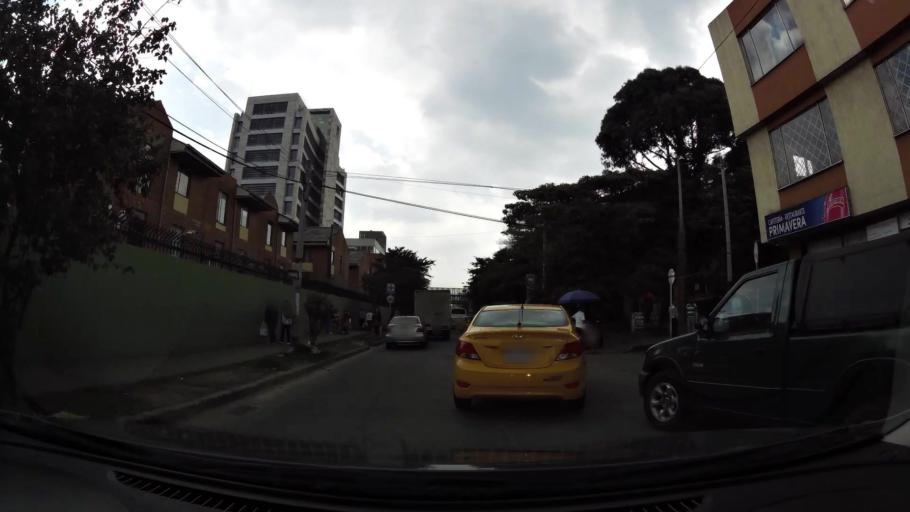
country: CO
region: Cundinamarca
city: La Calera
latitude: 4.7409
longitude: -74.0333
